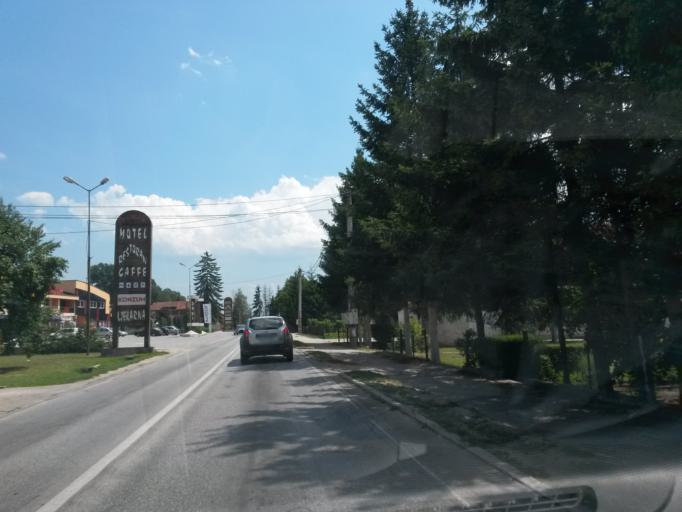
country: BA
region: Federation of Bosnia and Herzegovina
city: Vitez
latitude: 44.1907
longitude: 17.7360
